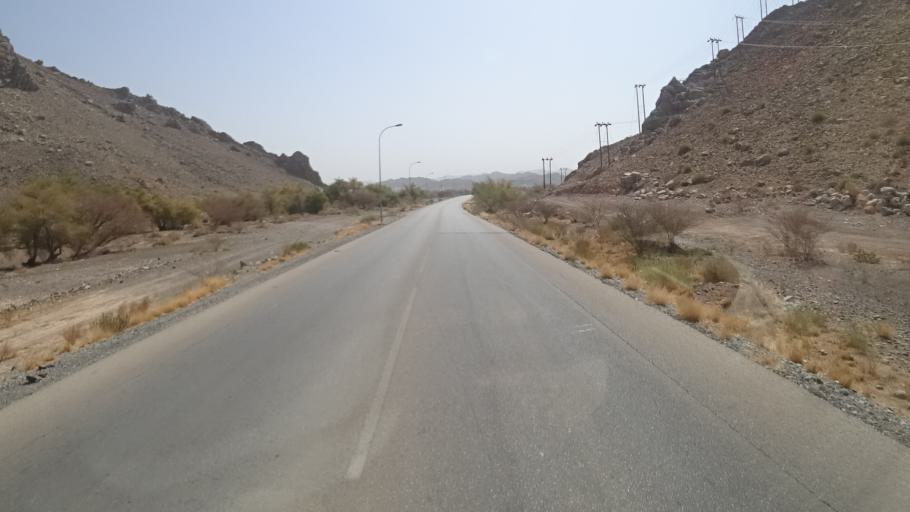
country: OM
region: Muhafazat ad Dakhiliyah
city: Bahla'
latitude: 23.0297
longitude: 57.3231
